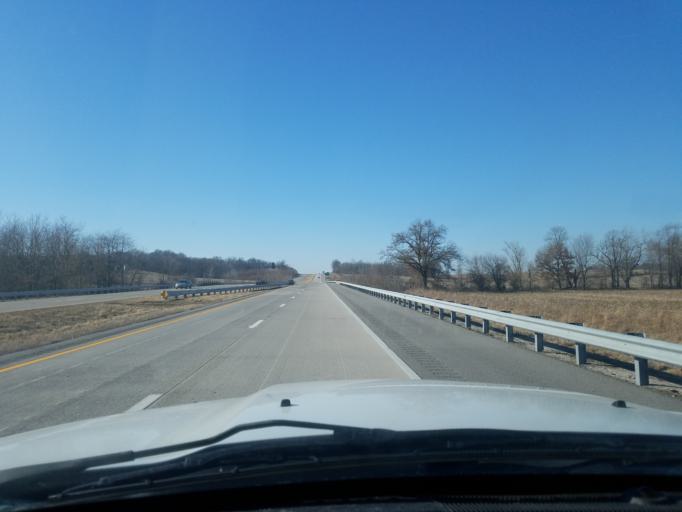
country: US
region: Kentucky
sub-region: Henderson County
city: Henderson
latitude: 37.7805
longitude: -87.4546
